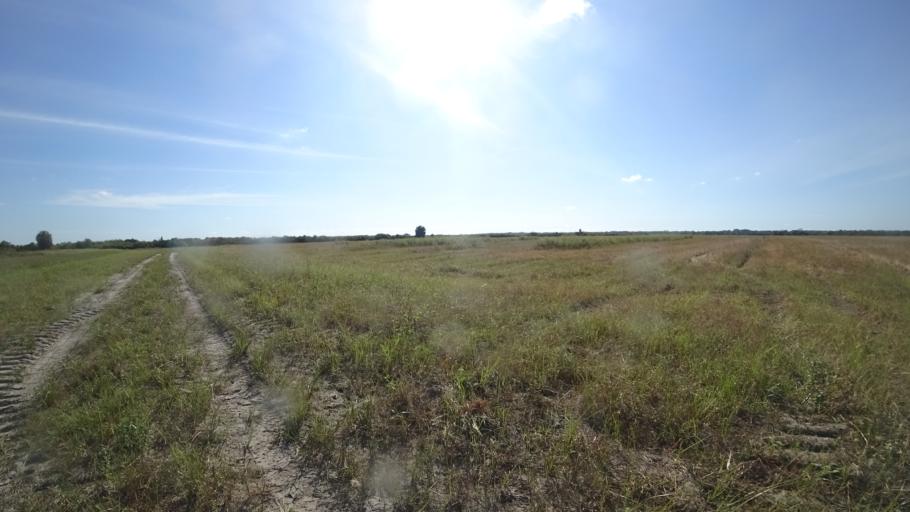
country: US
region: Florida
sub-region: Sarasota County
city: The Meadows
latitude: 27.4444
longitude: -82.3445
